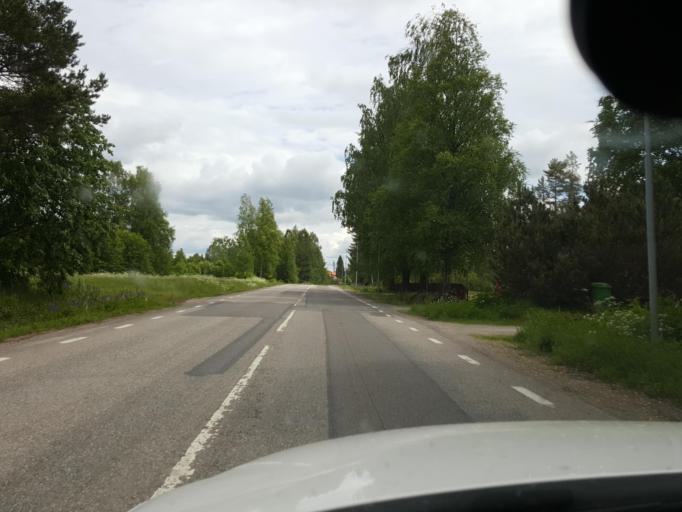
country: SE
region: Gaevleborg
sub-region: Ljusdals Kommun
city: Farila
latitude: 61.8094
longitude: 15.7621
